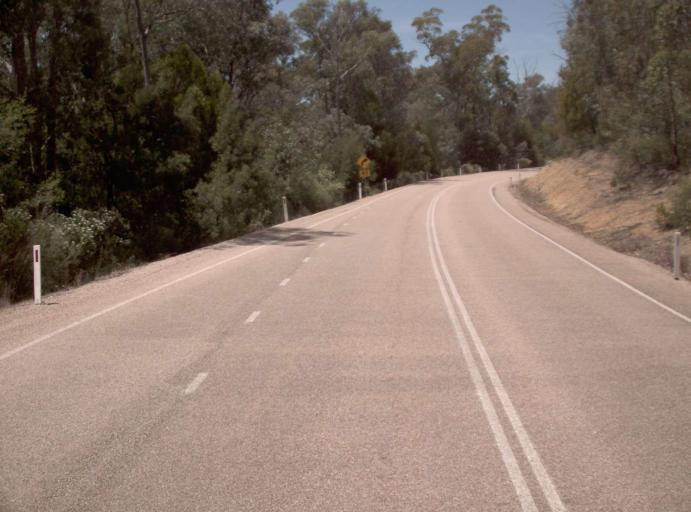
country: AU
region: Victoria
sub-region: East Gippsland
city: Lakes Entrance
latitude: -37.5649
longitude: 147.8886
